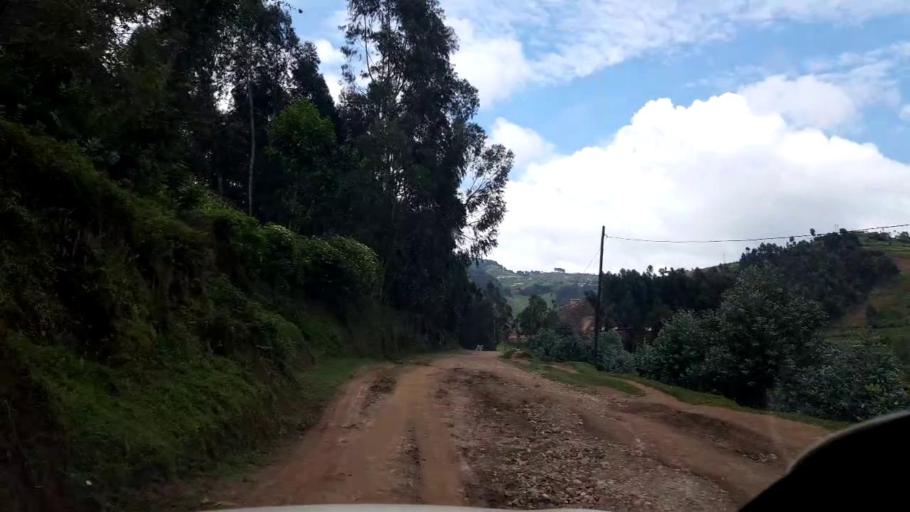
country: RW
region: Western Province
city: Kibuye
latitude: -1.9083
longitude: 29.4563
